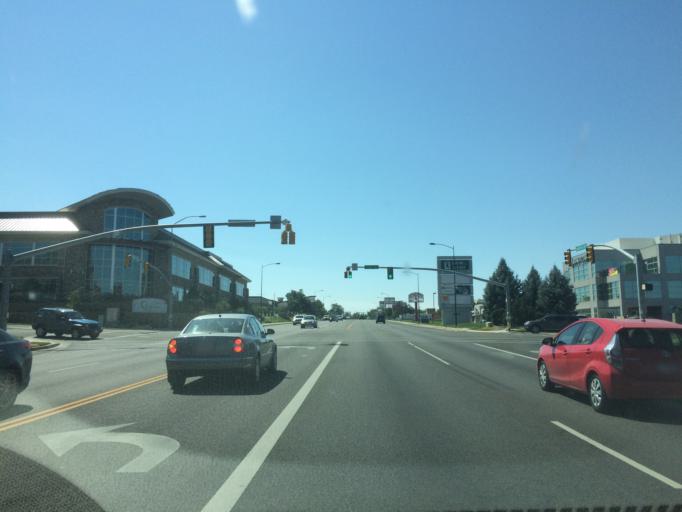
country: US
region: Utah
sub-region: Weber County
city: South Ogden
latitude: 41.1801
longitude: -111.9492
